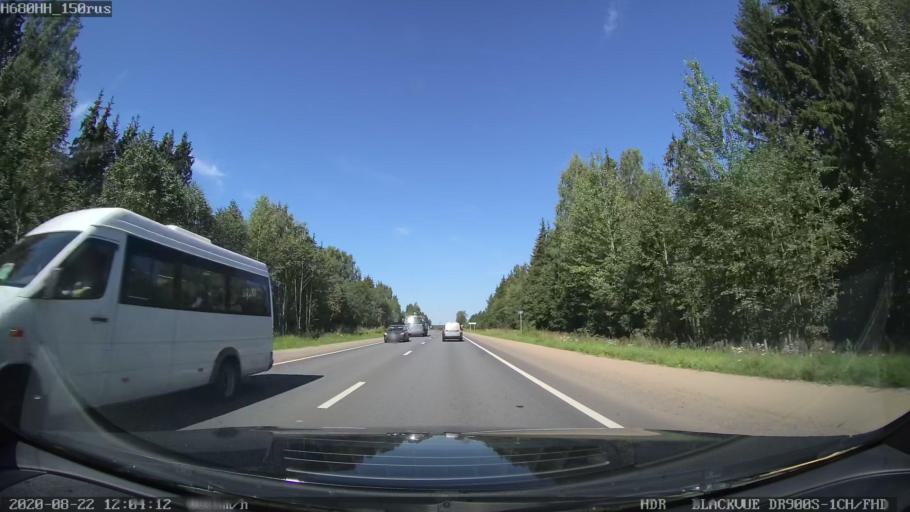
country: RU
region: Tverskaya
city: Rameshki
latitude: 57.2651
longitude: 36.0759
